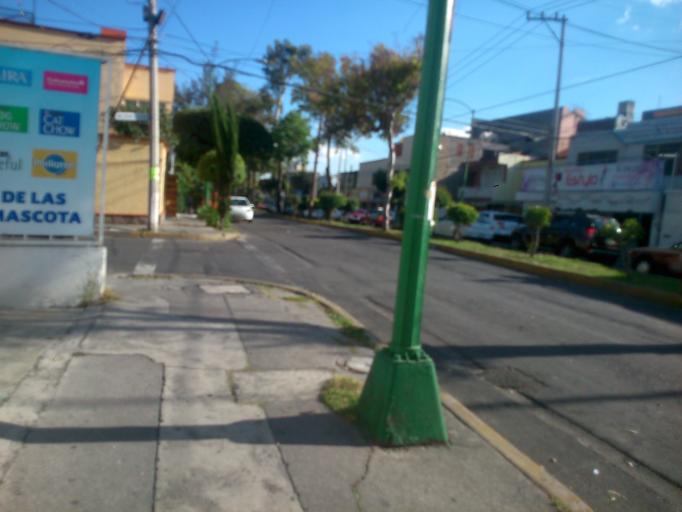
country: MX
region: Mexico
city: Colonia Lindavista
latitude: 19.4966
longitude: -99.1266
